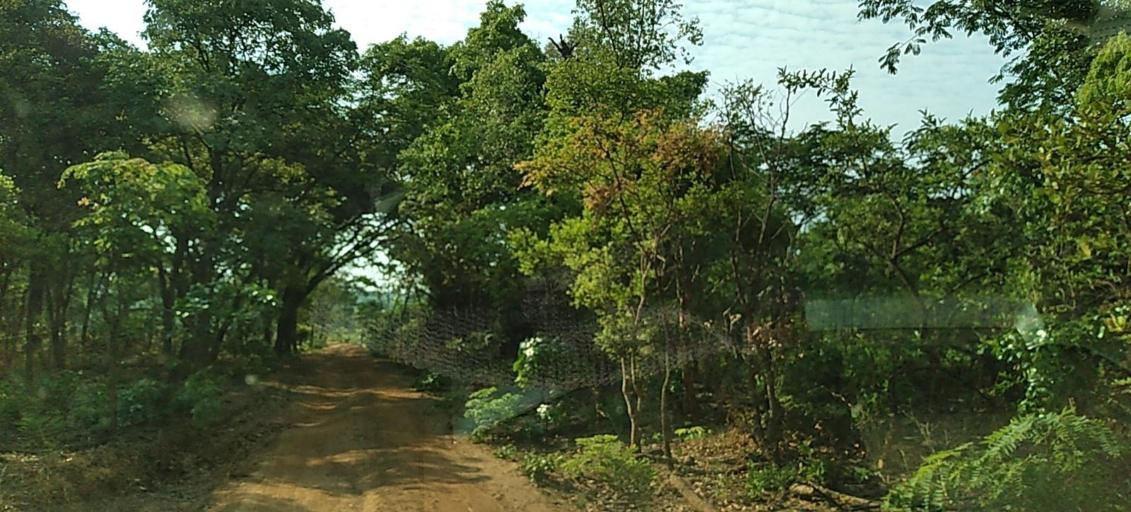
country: ZM
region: Copperbelt
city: Kalulushi
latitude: -13.0045
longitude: 27.7157
